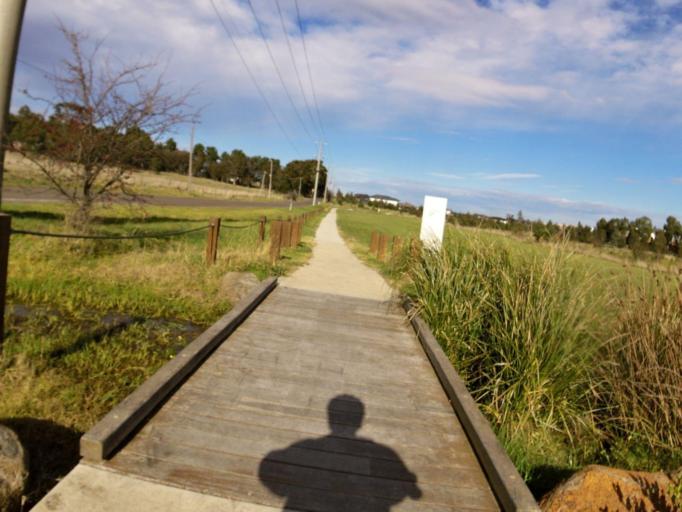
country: AU
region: Victoria
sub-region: Whittlesea
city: Epping
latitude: -37.6171
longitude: 145.0436
